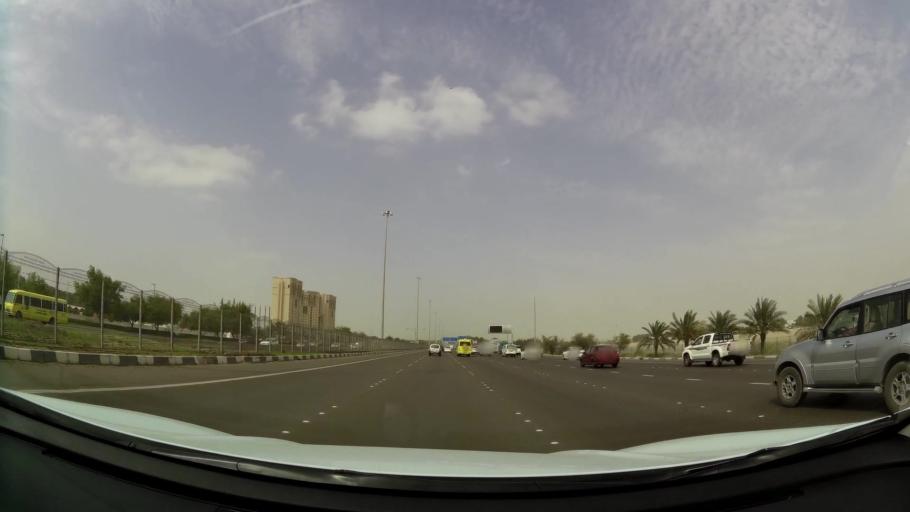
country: AE
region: Abu Dhabi
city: Abu Dhabi
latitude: 24.3795
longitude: 54.5248
